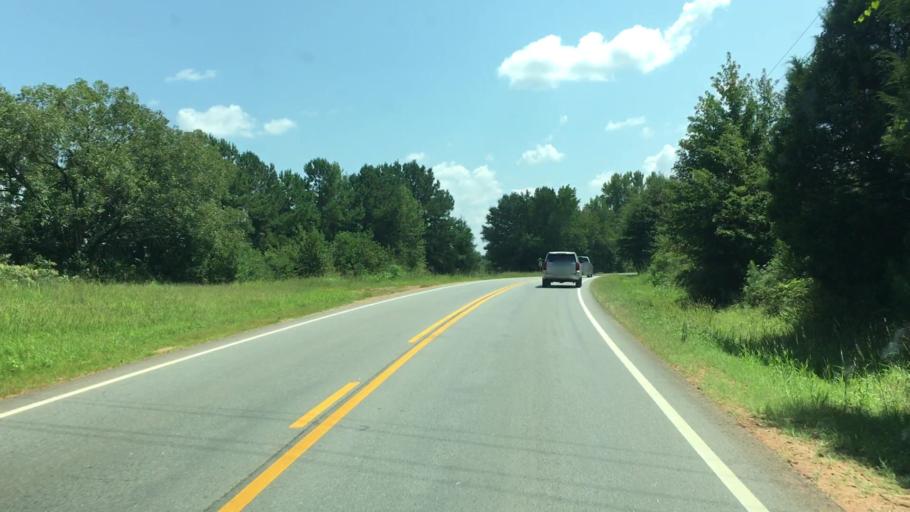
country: US
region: Georgia
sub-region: Oconee County
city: Watkinsville
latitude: 33.7857
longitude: -83.4231
